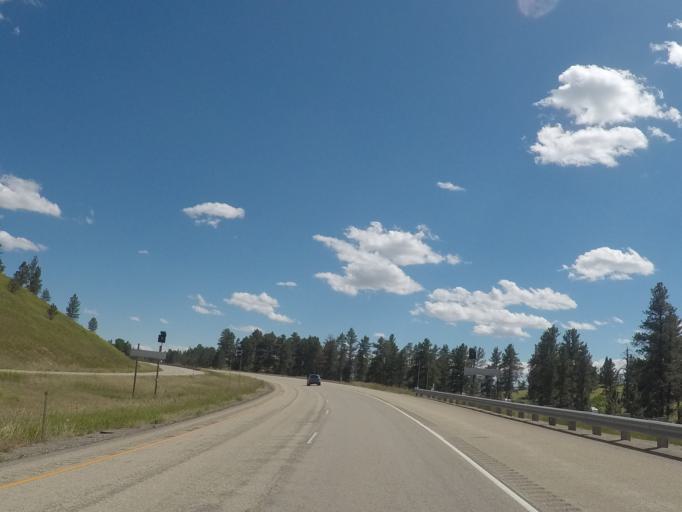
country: US
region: Montana
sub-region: Big Horn County
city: Crow Agency
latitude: 45.3430
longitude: -107.3543
